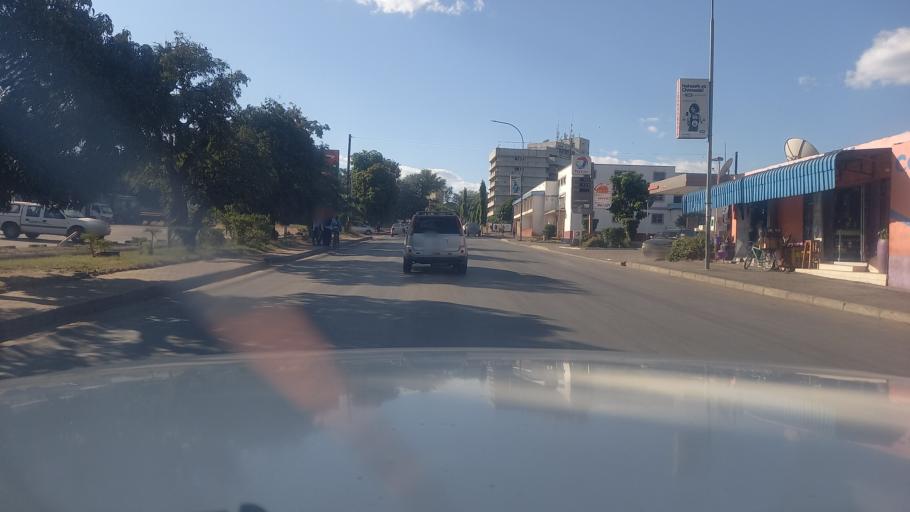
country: ZM
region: Southern
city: Livingstone
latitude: -17.8511
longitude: 25.8552
